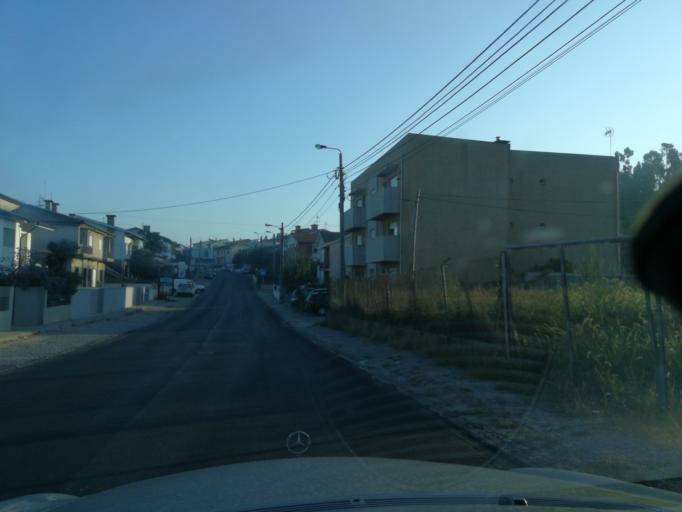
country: PT
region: Braga
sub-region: Braga
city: Braga
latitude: 41.5253
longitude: -8.4291
